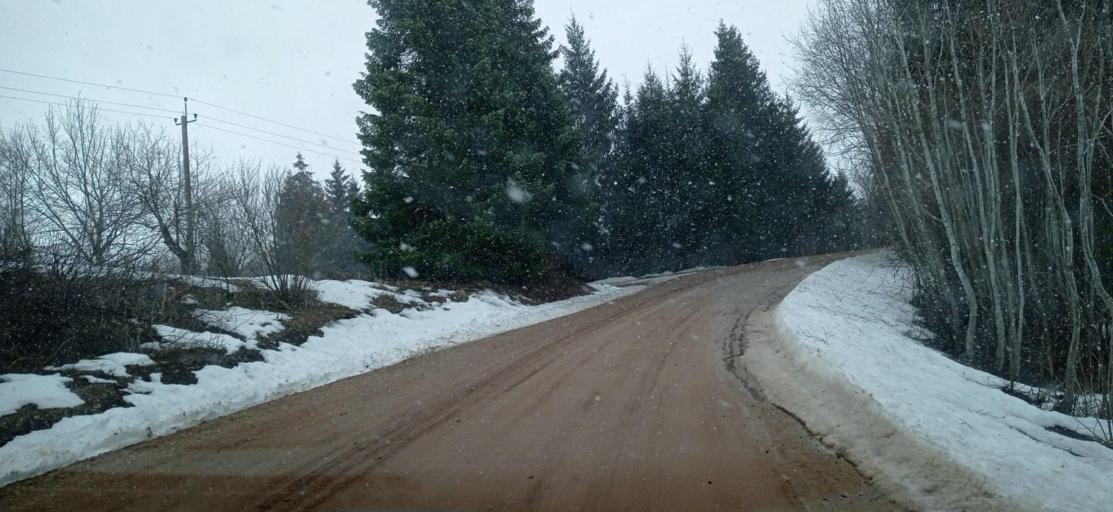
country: EE
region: Tartu
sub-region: UElenurme vald
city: Ulenurme
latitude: 58.1200
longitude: 26.7001
